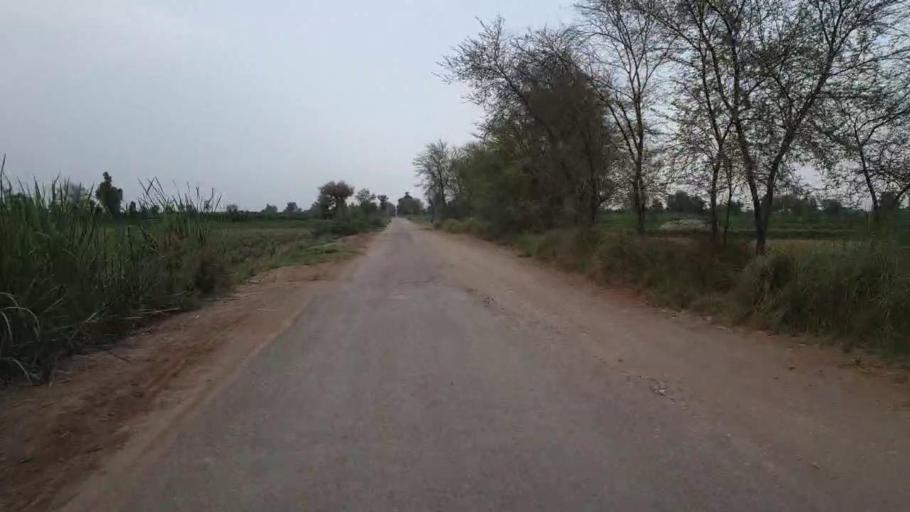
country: PK
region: Sindh
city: Bandhi
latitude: 26.5281
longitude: 68.1944
